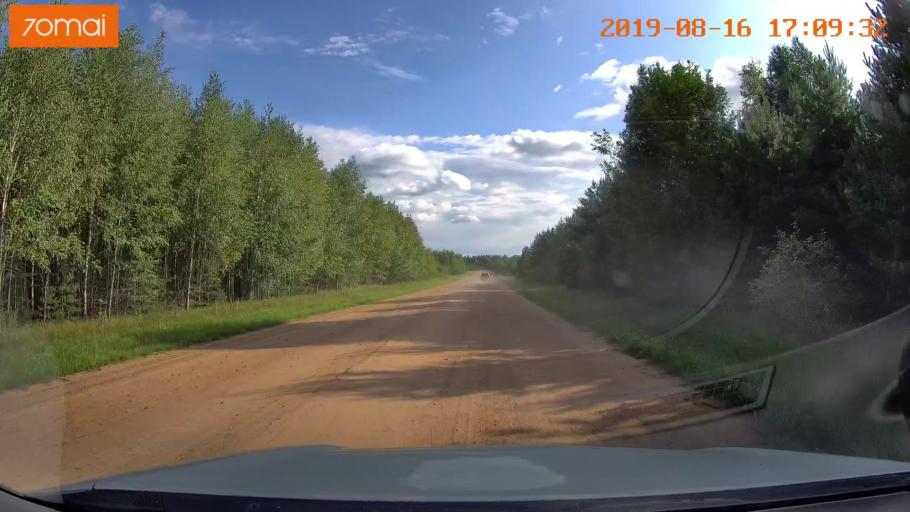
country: BY
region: Mogilev
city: Hlusha
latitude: 53.2119
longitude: 28.9243
